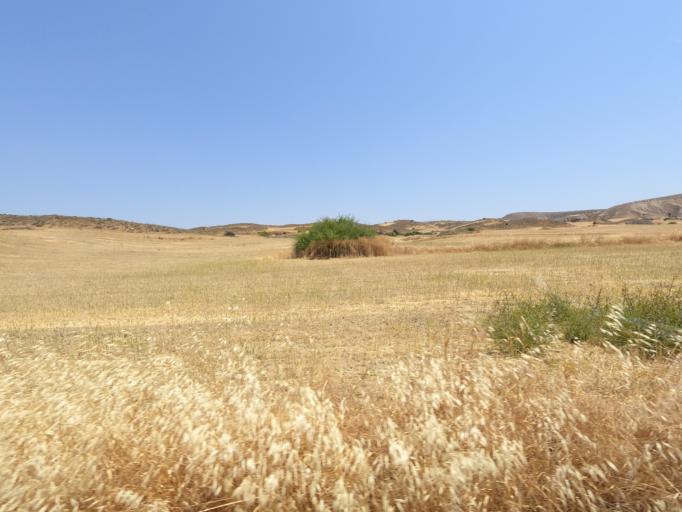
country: CY
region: Larnaka
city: Troulloi
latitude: 35.0196
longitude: 33.6388
